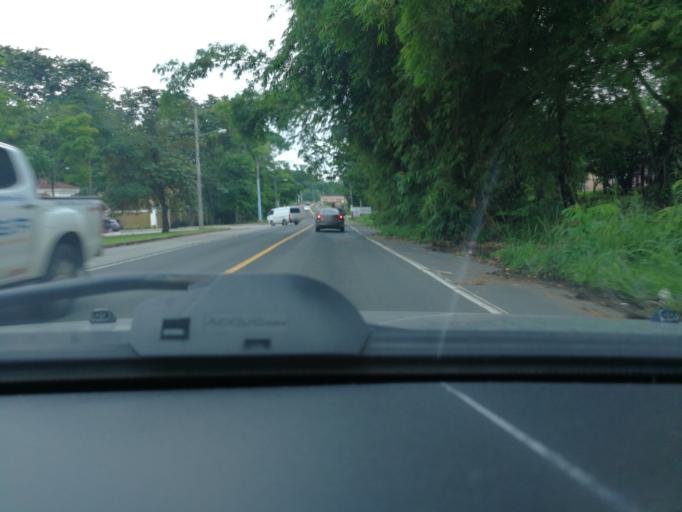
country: PA
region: Panama
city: Panama
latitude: 9.0086
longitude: -79.5444
